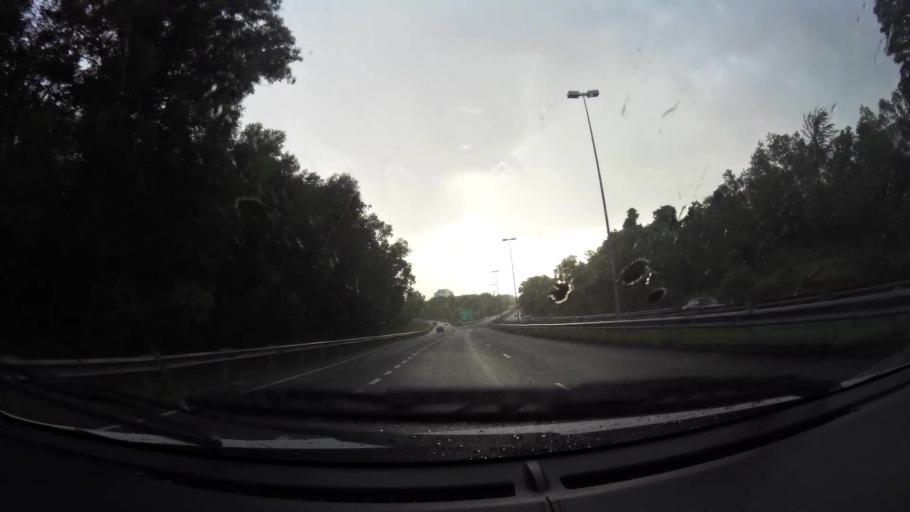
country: BN
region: Brunei and Muara
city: Bandar Seri Begawan
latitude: 4.9267
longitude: 114.9653
